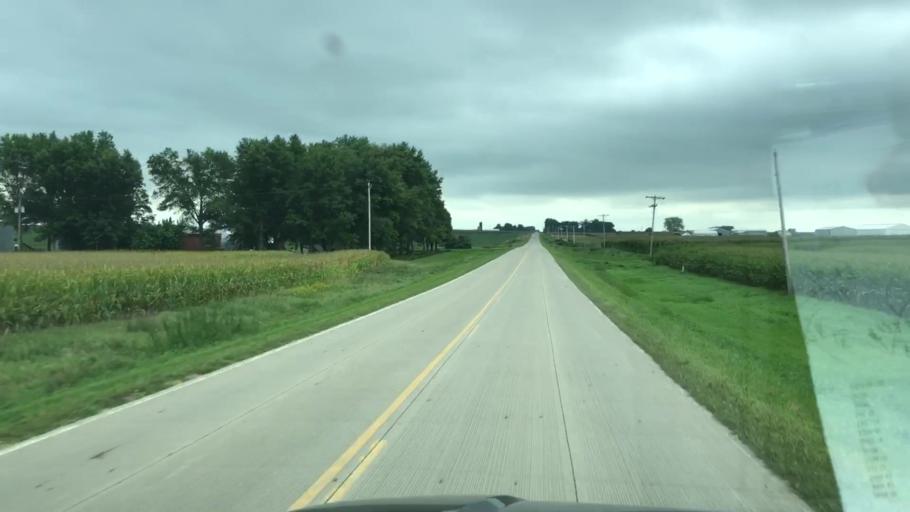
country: US
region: Iowa
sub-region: Sioux County
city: Alton
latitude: 43.1069
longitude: -95.9786
